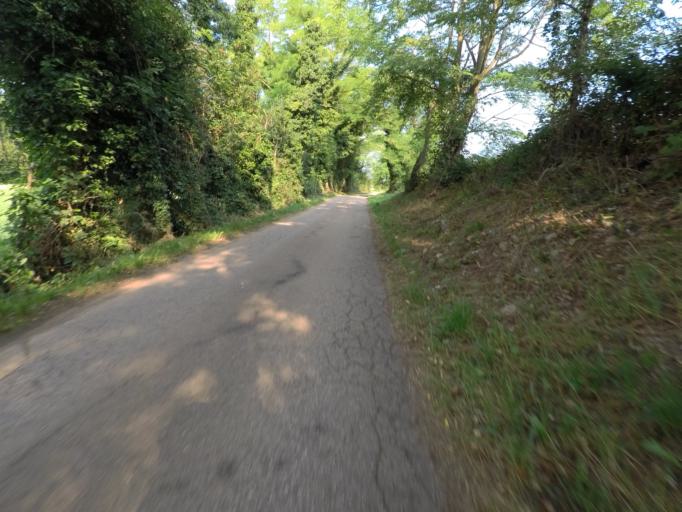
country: IT
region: Friuli Venezia Giulia
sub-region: Provincia di Pordenone
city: Meduno
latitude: 46.2043
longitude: 12.8197
